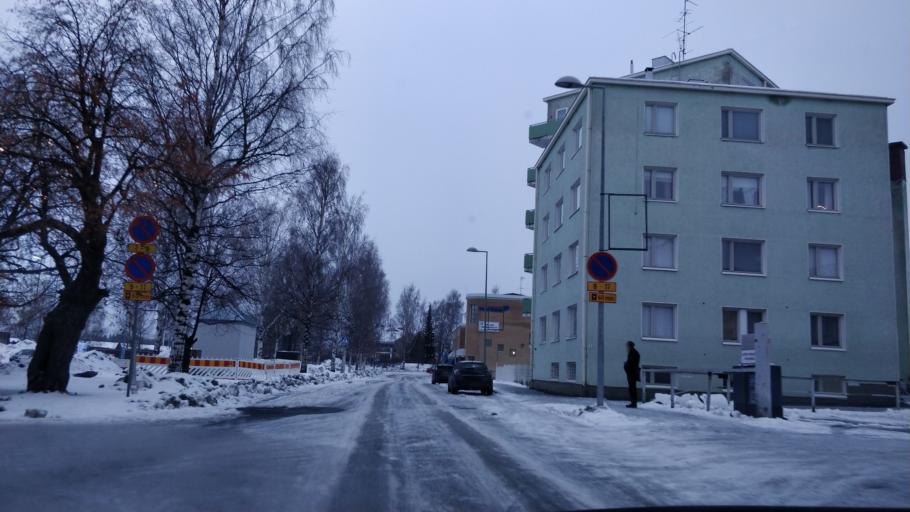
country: FI
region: Lapland
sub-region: Kemi-Tornio
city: Kemi
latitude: 65.7377
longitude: 24.5616
